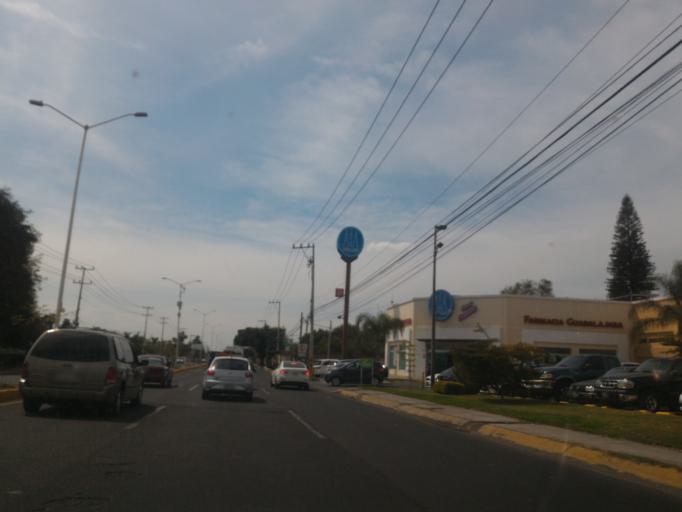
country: MX
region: Jalisco
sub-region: Tlajomulco de Zuniga
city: La Tijera
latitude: 20.5699
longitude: -103.4402
